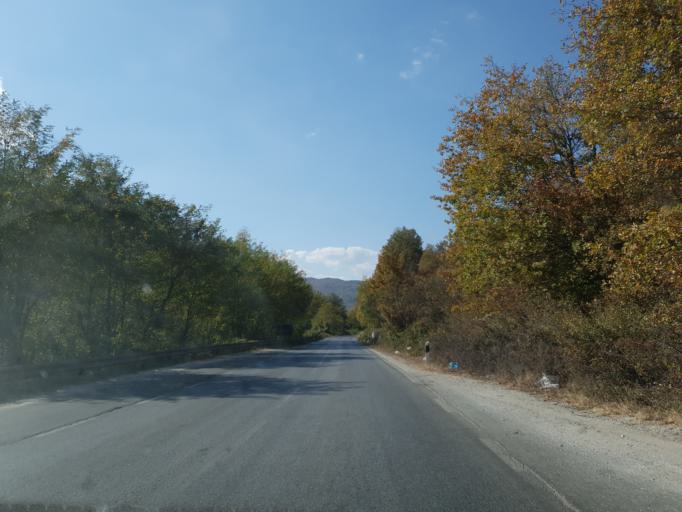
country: MK
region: Vranestica
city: Vranestica
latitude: 41.4685
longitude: 21.0166
